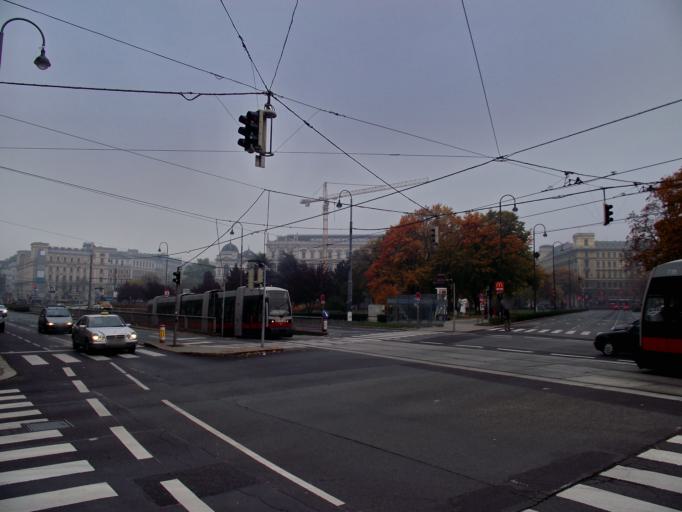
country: AT
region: Vienna
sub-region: Wien Stadt
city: Vienna
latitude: 48.2150
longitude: 16.3616
